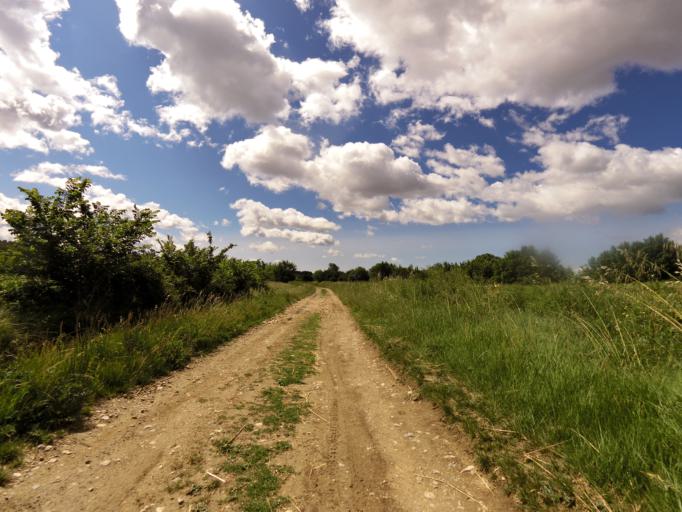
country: FR
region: Languedoc-Roussillon
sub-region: Departement du Gard
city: Vergeze
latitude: 43.7632
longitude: 4.2128
